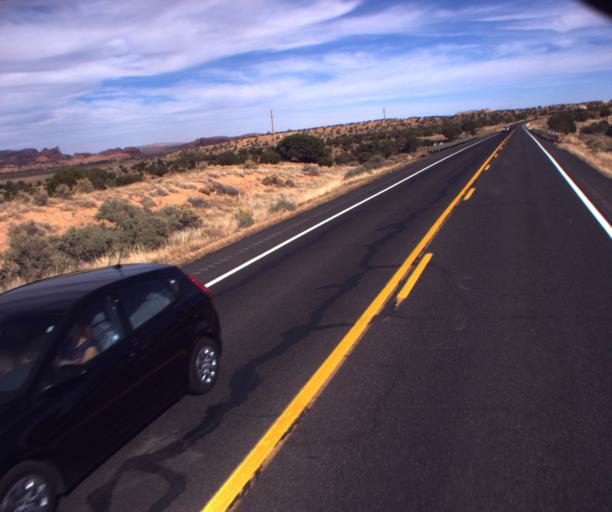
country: US
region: Arizona
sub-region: Navajo County
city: Kayenta
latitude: 36.6975
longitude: -110.3415
